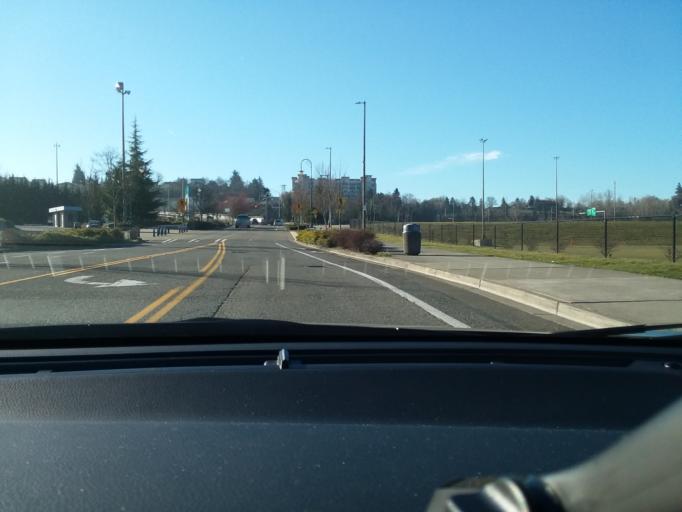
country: US
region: Washington
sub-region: Pierce County
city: Tacoma
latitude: 47.2369
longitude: -122.4287
